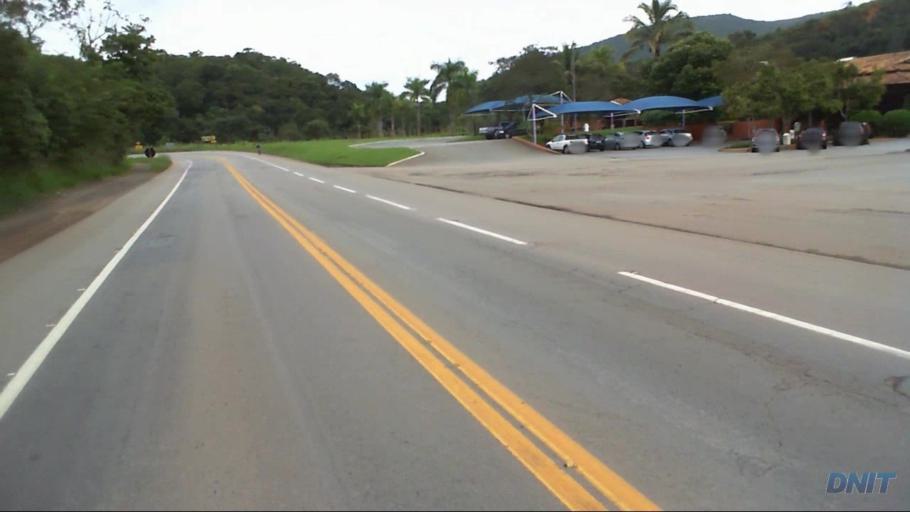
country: BR
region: Minas Gerais
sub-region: Barao De Cocais
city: Barao de Cocais
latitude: -19.8332
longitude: -43.3513
